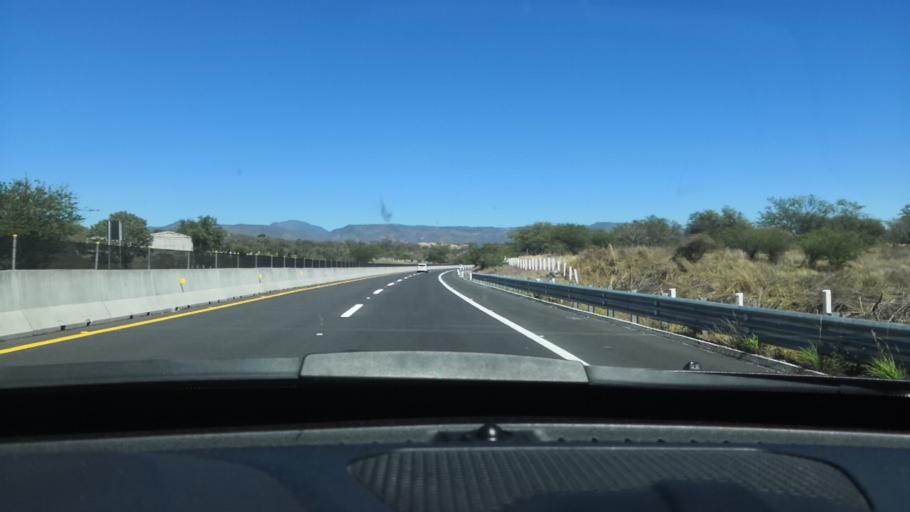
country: MX
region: Nayarit
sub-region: Ahuacatlan
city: Ahuacatlan
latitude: 21.0635
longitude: -104.5033
